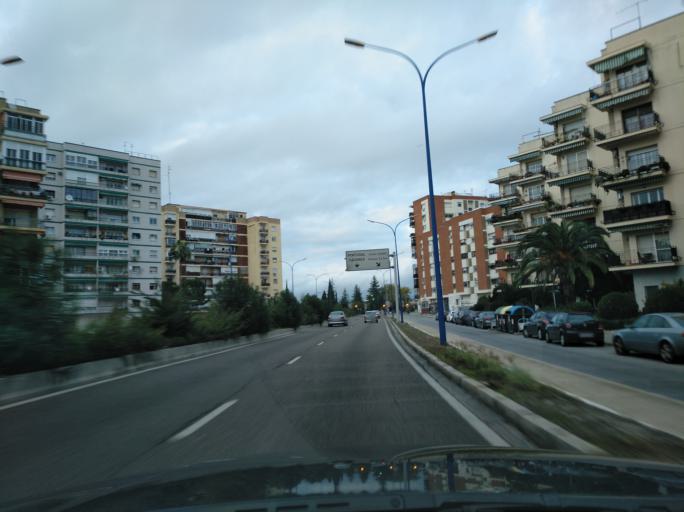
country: ES
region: Extremadura
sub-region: Provincia de Badajoz
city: Badajoz
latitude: 38.8761
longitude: -6.9812
